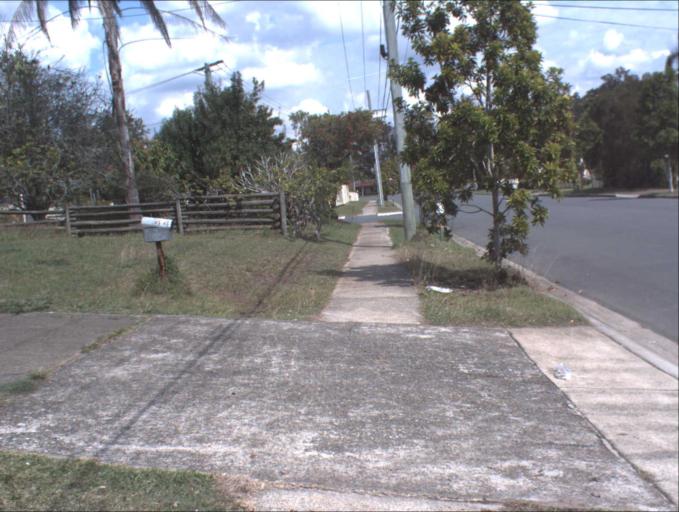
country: AU
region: Queensland
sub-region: Brisbane
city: Sunnybank Hills
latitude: -27.6561
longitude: 153.0456
